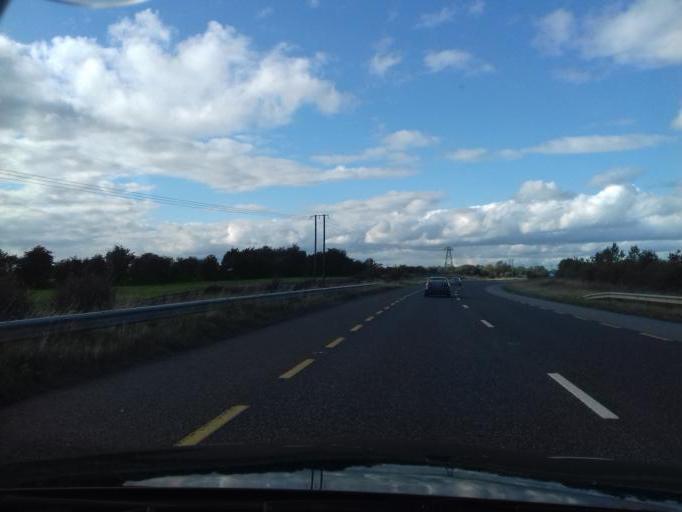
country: IE
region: Leinster
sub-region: Uibh Fhaili
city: Tullamore
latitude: 53.2722
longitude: -7.4651
